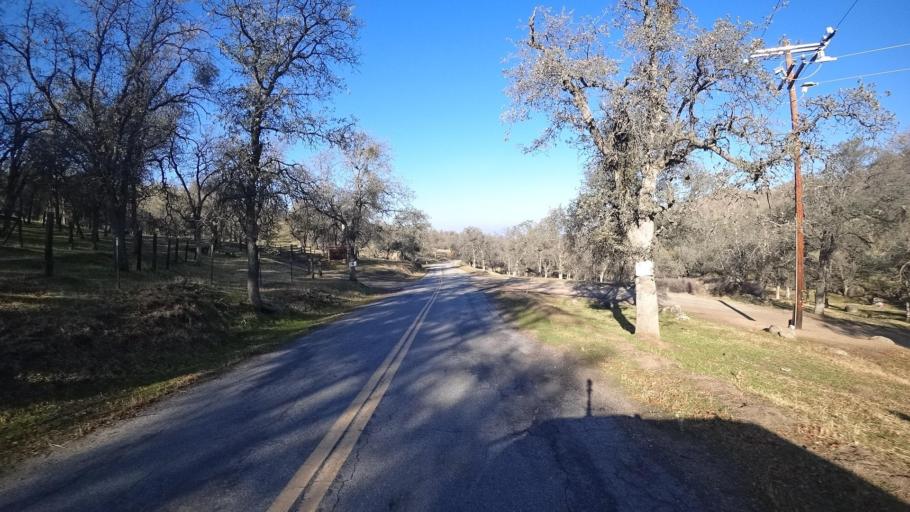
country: US
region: California
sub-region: Kern County
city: Alta Sierra
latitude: 35.7674
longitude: -118.8240
